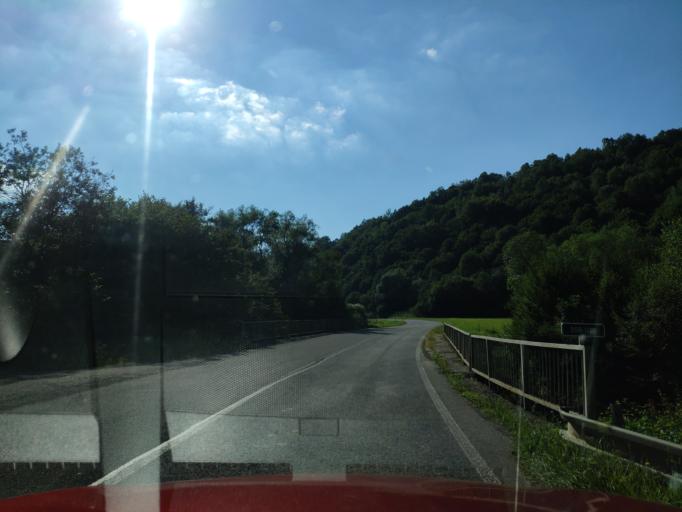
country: SK
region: Presovsky
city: Snina
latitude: 49.0372
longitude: 22.2559
